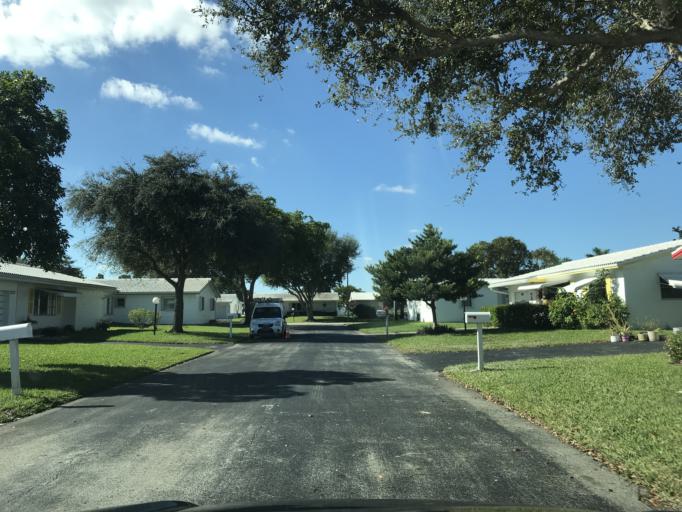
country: US
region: Florida
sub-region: Broward County
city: Plantation
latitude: 26.1423
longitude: -80.2616
